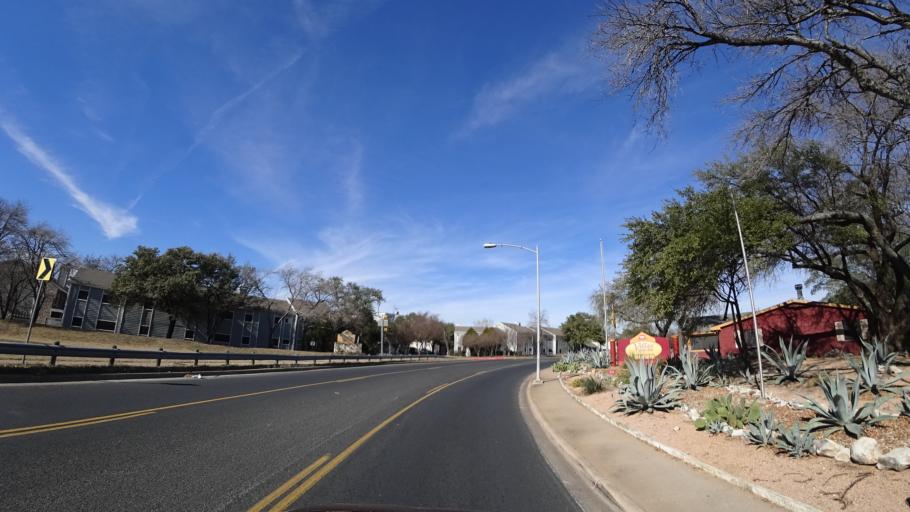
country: US
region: Texas
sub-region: Travis County
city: Wells Branch
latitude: 30.3728
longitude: -97.7125
